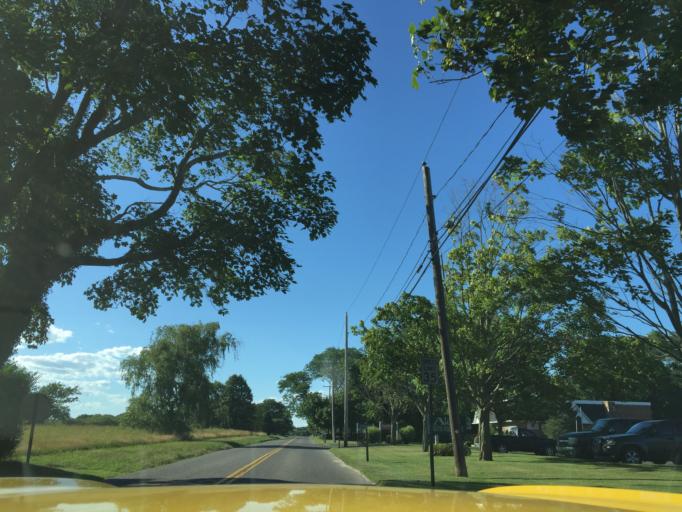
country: US
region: New York
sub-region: Suffolk County
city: Southold
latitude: 41.0648
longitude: -72.4335
